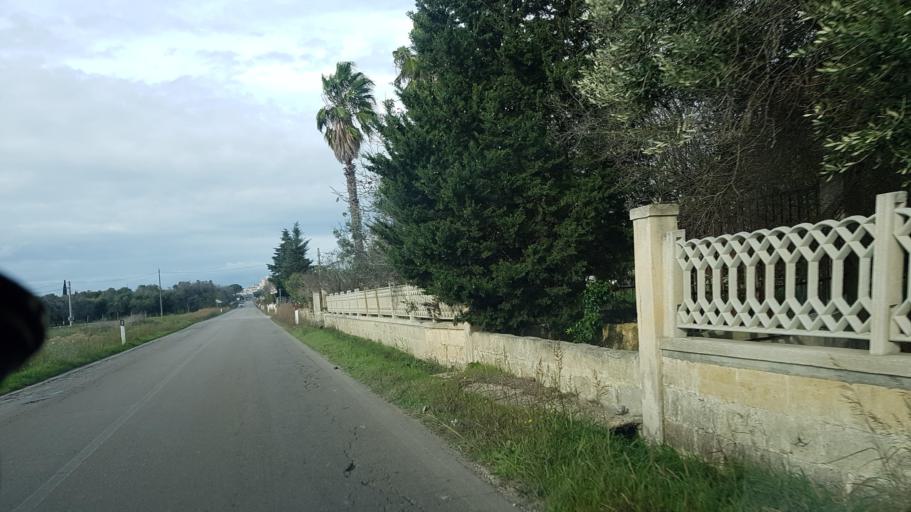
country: IT
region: Apulia
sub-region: Provincia di Brindisi
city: Oria
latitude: 40.4893
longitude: 17.6642
